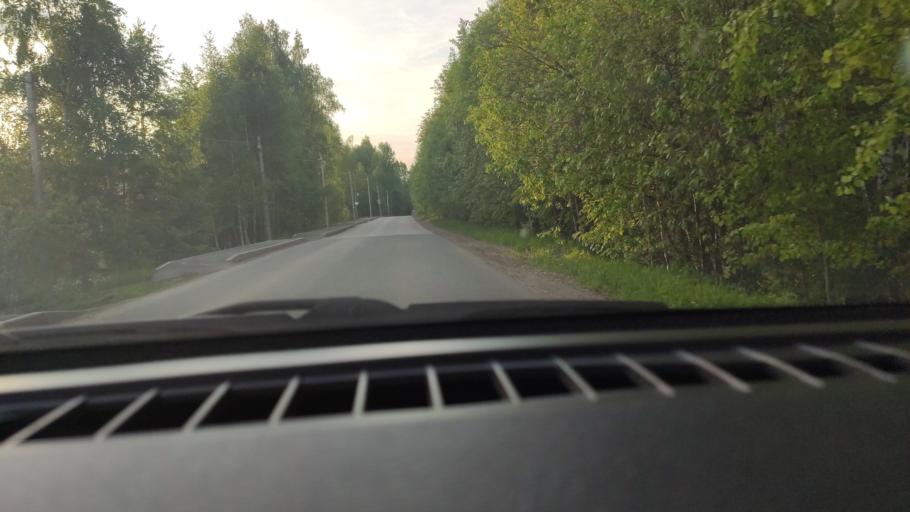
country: RU
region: Perm
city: Kondratovo
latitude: 58.0590
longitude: 56.0053
